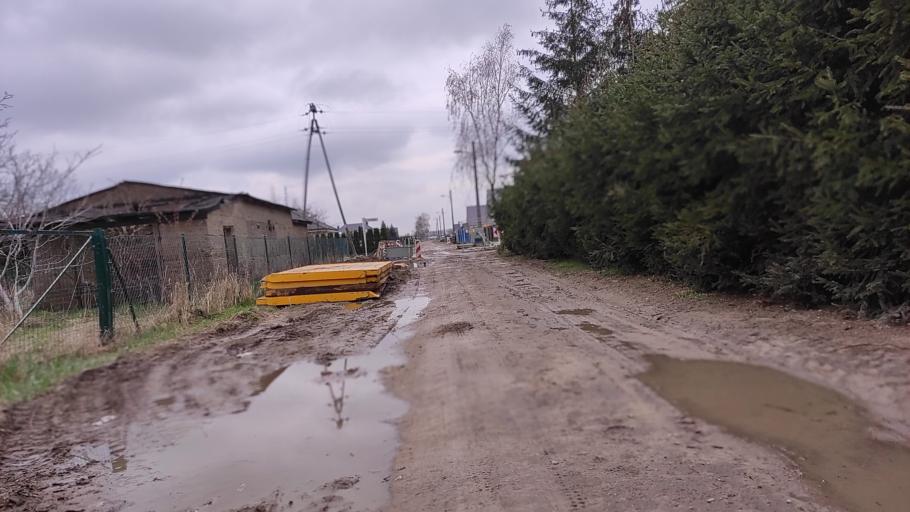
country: PL
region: Greater Poland Voivodeship
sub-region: Powiat poznanski
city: Kostrzyn
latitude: 52.4042
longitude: 17.1732
